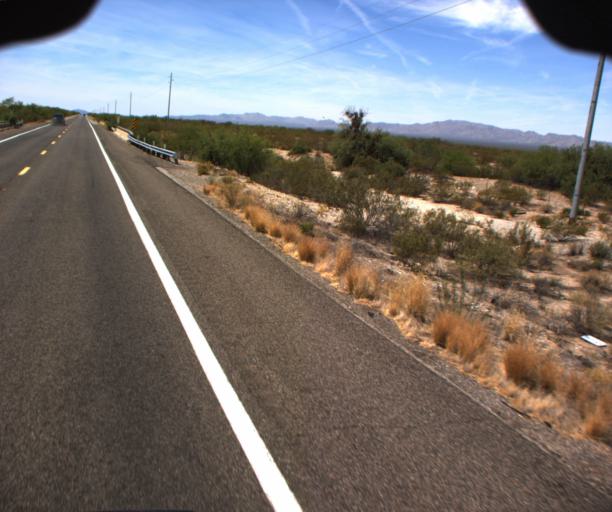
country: US
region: Arizona
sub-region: La Paz County
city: Salome
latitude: 33.8750
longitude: -113.3796
